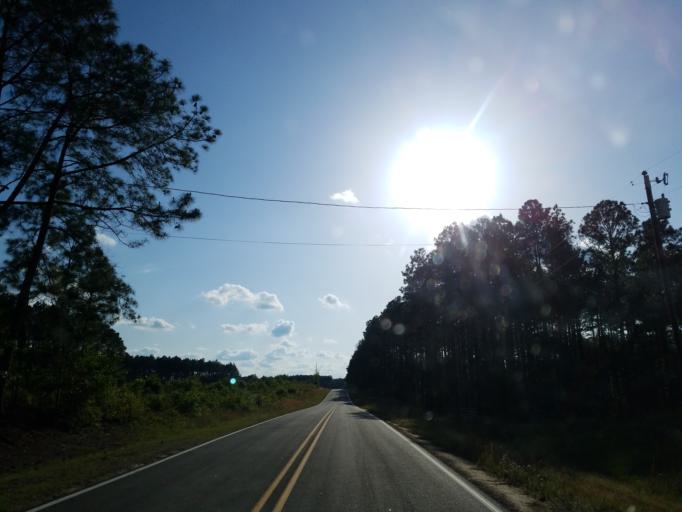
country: US
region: Georgia
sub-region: Turner County
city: Ashburn
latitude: 31.6094
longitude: -83.5786
